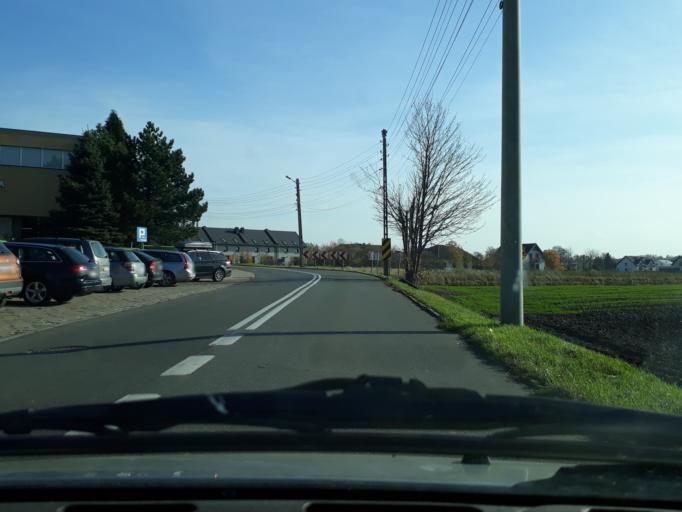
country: PL
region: Silesian Voivodeship
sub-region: Powiat tarnogorski
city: Tarnowskie Gory
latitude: 50.4256
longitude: 18.8485
